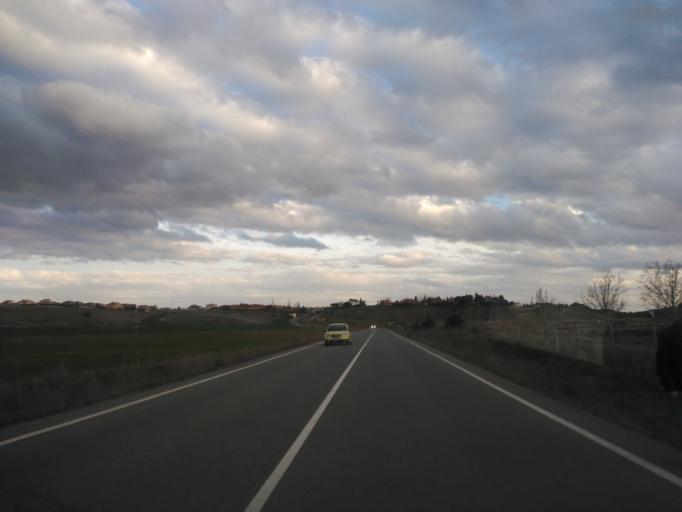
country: ES
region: Castille and Leon
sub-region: Provincia de Salamanca
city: Carbajosa de la Sagrada
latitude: 40.9325
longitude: -5.6428
